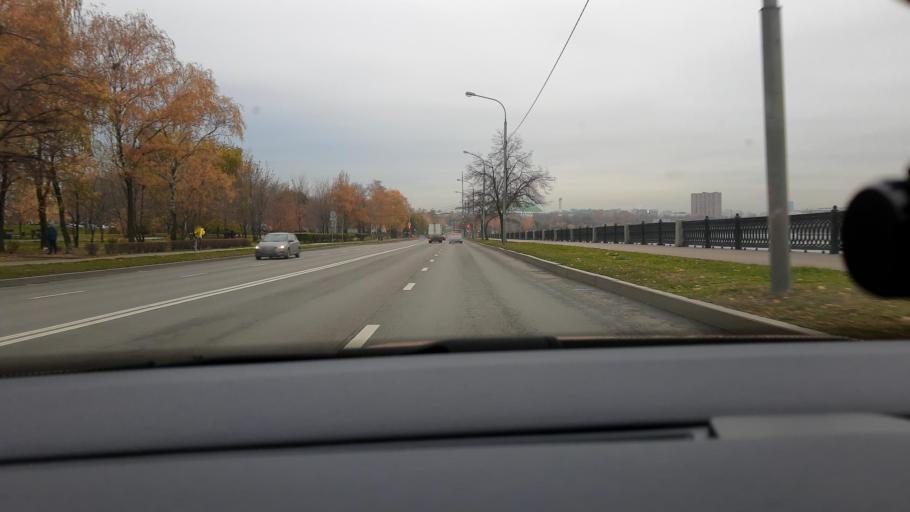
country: RU
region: Moskovskaya
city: Kozhukhovo
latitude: 55.6839
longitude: 37.6458
